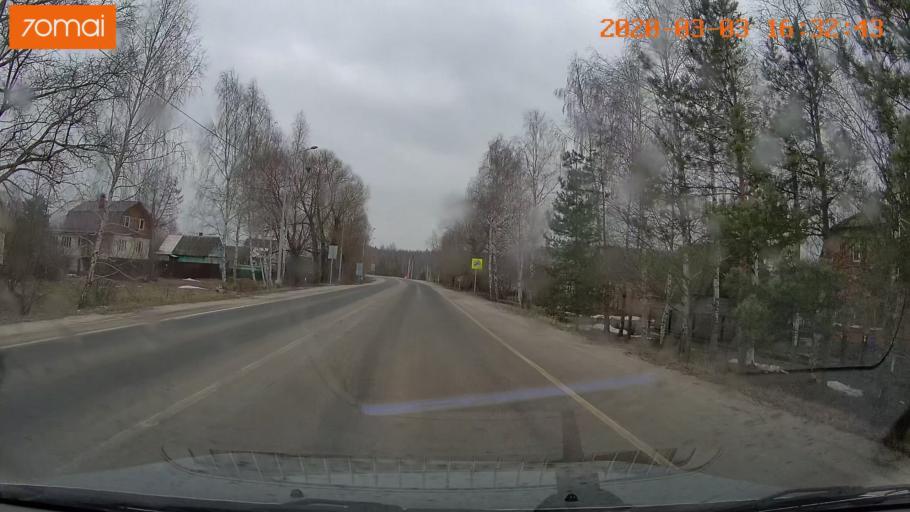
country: RU
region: Moskovskaya
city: Konobeyevo
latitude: 55.4194
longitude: 38.7345
